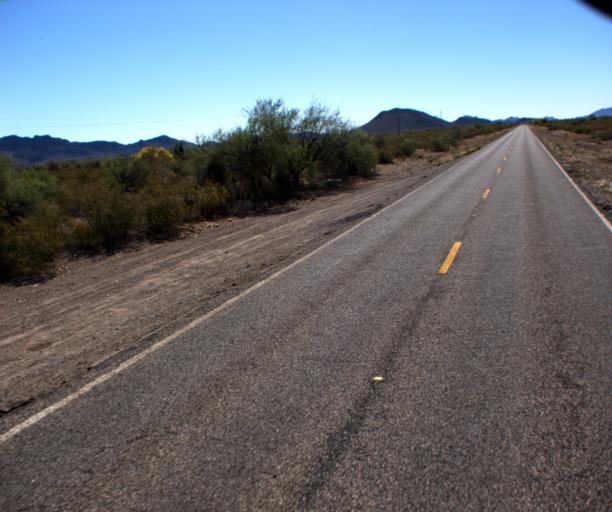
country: US
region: Arizona
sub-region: Pima County
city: Ajo
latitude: 32.3059
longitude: -112.7601
